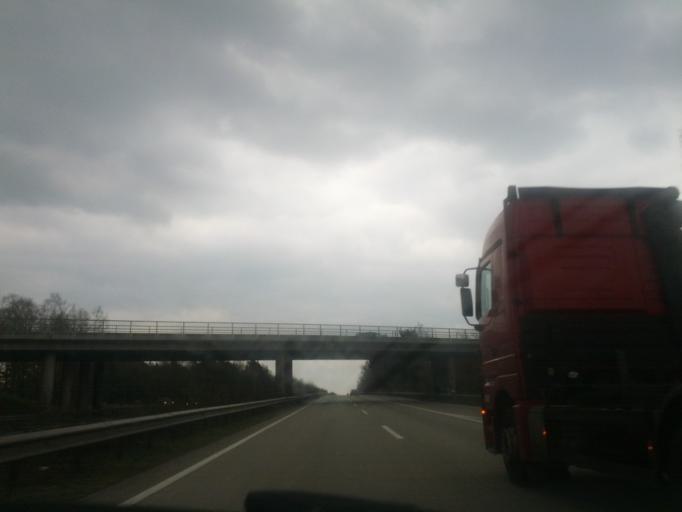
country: DE
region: Lower Saxony
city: Verden
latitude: 52.9598
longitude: 9.2445
